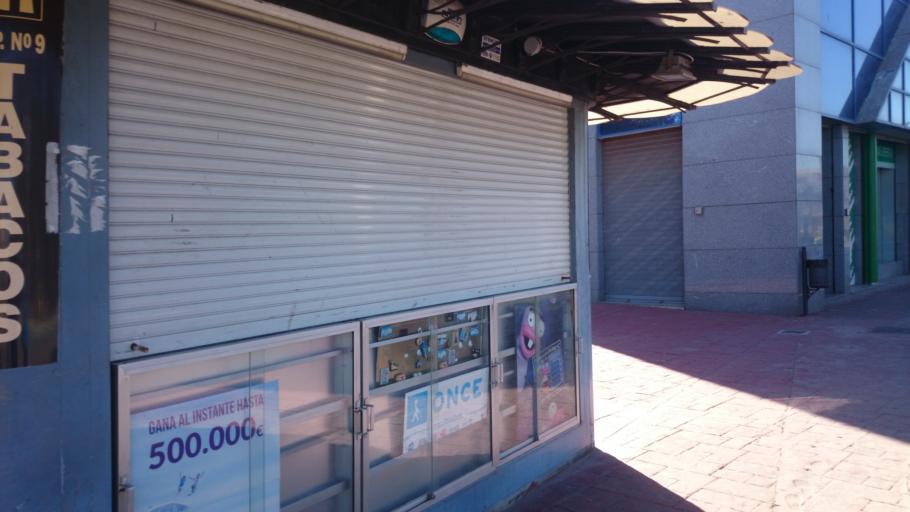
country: ES
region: Ceuta
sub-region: Ceuta
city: Ceuta
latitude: 35.8909
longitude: -5.3177
